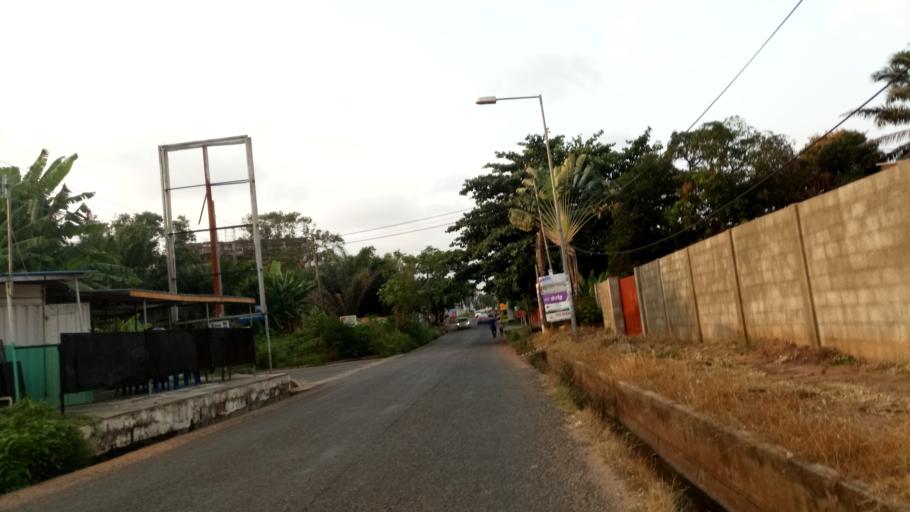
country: GH
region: Greater Accra
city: Accra
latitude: 5.5642
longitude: -0.1873
